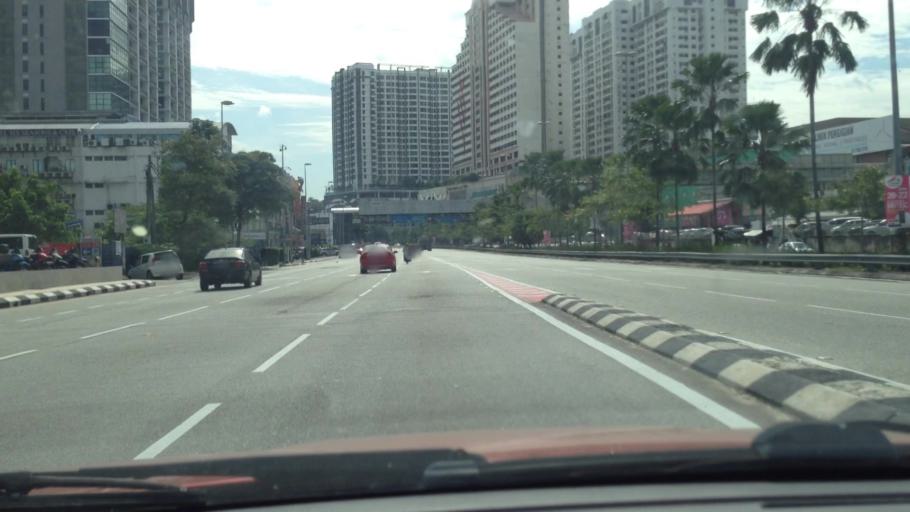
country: MY
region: Kuala Lumpur
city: Kuala Lumpur
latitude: 3.0833
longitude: 101.6702
